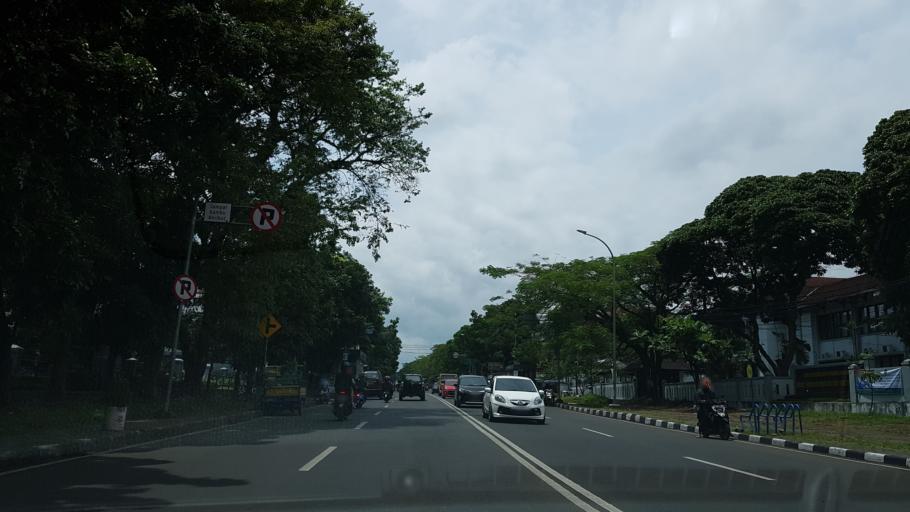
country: ID
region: West Java
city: Bandung
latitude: -6.8992
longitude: 107.6232
